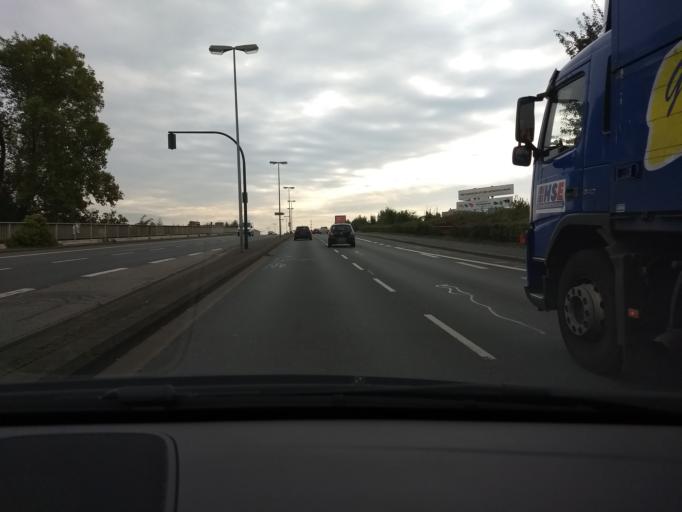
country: DE
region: North Rhine-Westphalia
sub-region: Regierungsbezirk Dusseldorf
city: Essen
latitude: 51.4671
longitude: 7.0251
